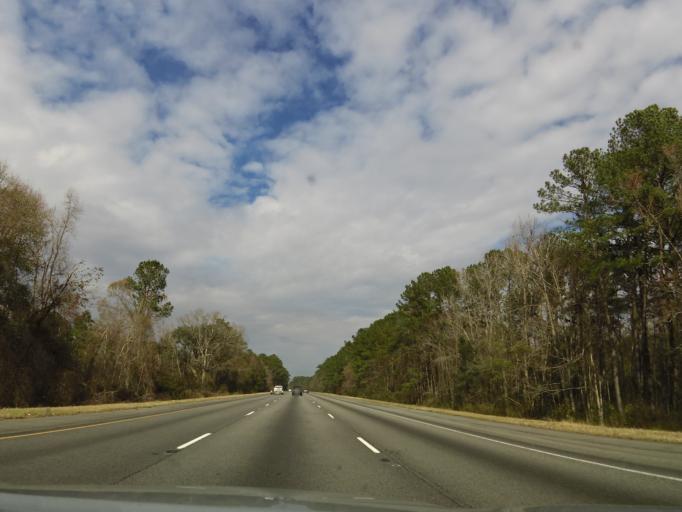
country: US
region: Georgia
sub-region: Bryan County
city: Richmond Hill
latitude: 31.8900
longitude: -81.3258
